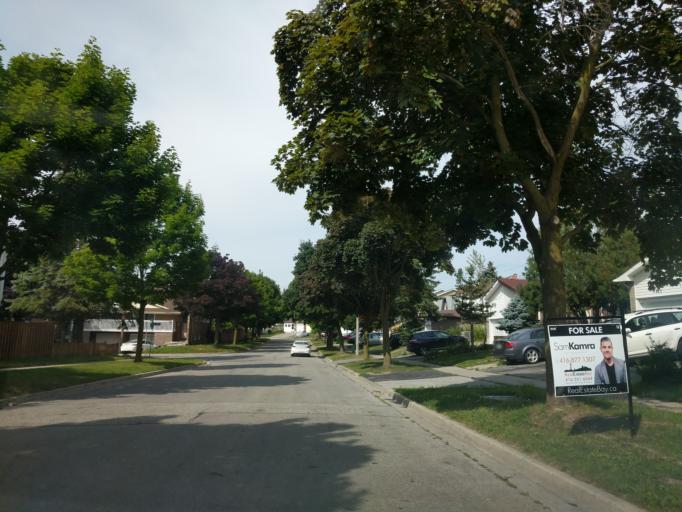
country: CA
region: Ontario
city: Scarborough
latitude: 43.8121
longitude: -79.2885
